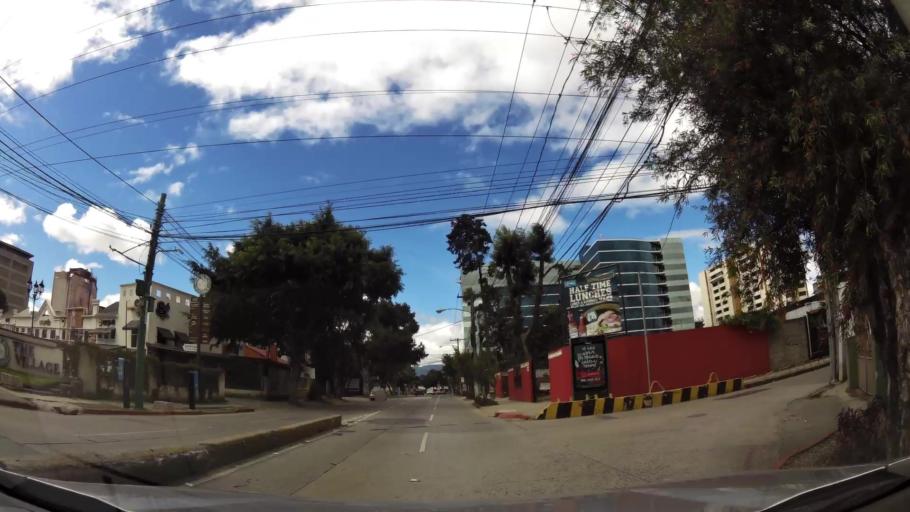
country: GT
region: Guatemala
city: Guatemala City
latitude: 14.6036
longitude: -90.5139
